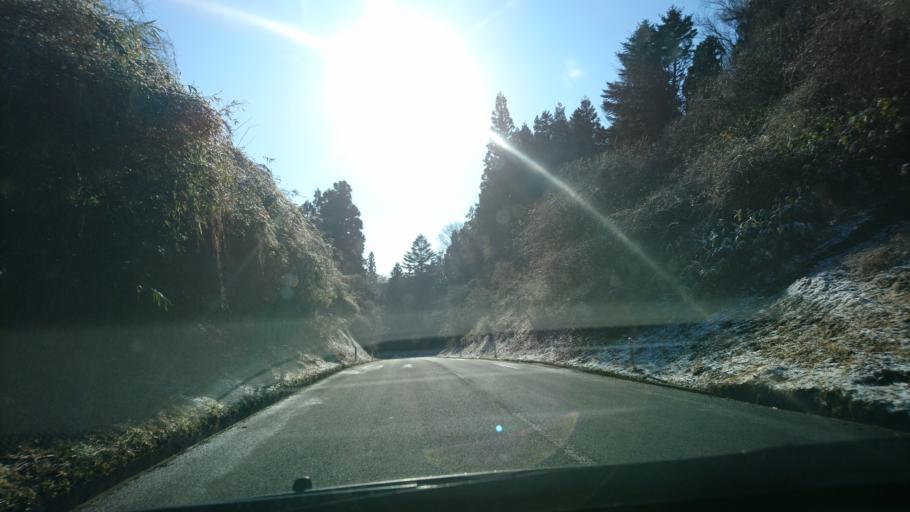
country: JP
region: Iwate
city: Ichinoseki
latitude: 38.8768
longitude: 141.3287
